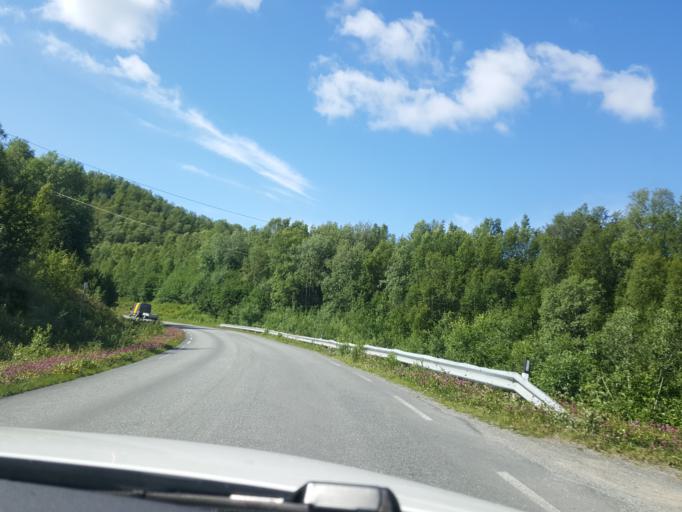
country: NO
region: Nordland
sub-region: Bodo
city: Loding
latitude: 67.1117
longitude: 15.0031
